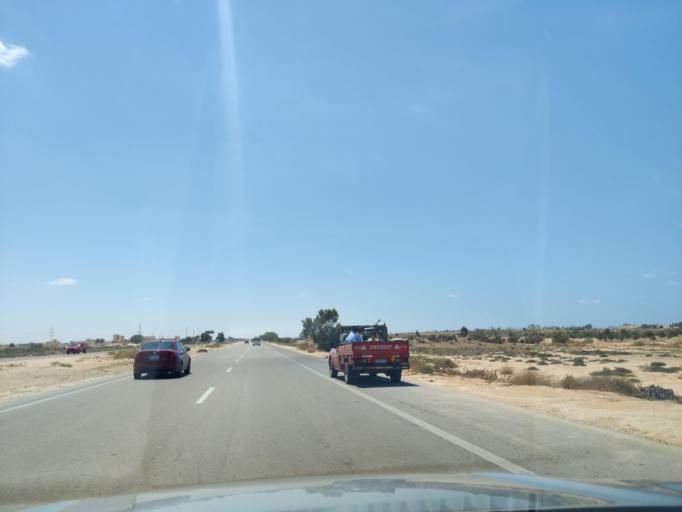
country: EG
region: Muhafazat Matruh
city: Al `Alamayn
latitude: 31.0697
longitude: 28.1351
